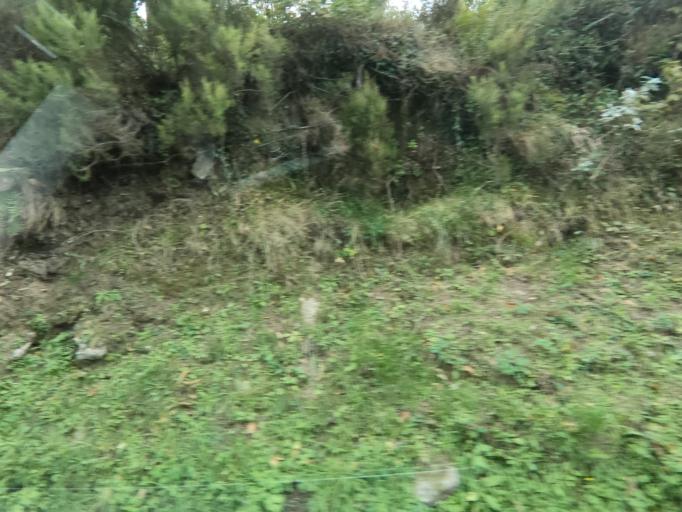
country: PT
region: Vila Real
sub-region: Vila Real
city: Vila Real
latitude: 41.3639
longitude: -7.8395
